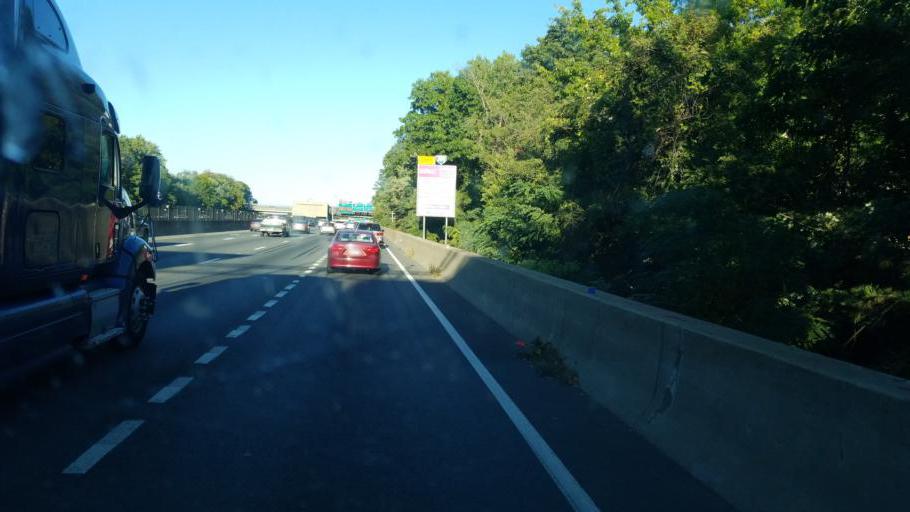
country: US
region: Virginia
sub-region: Fairfax County
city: Merrifield
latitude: 38.8817
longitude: -77.2325
